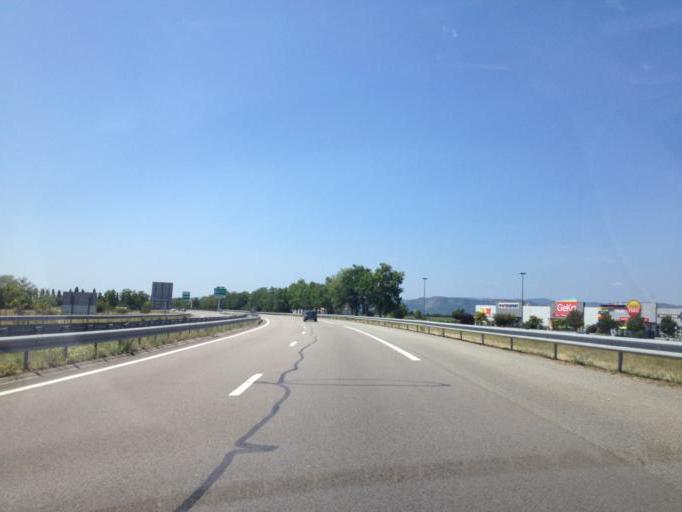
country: FR
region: Rhone-Alpes
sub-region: Departement de la Drome
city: Saint-Marcel-les-Valence
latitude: 44.9595
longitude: 4.9388
